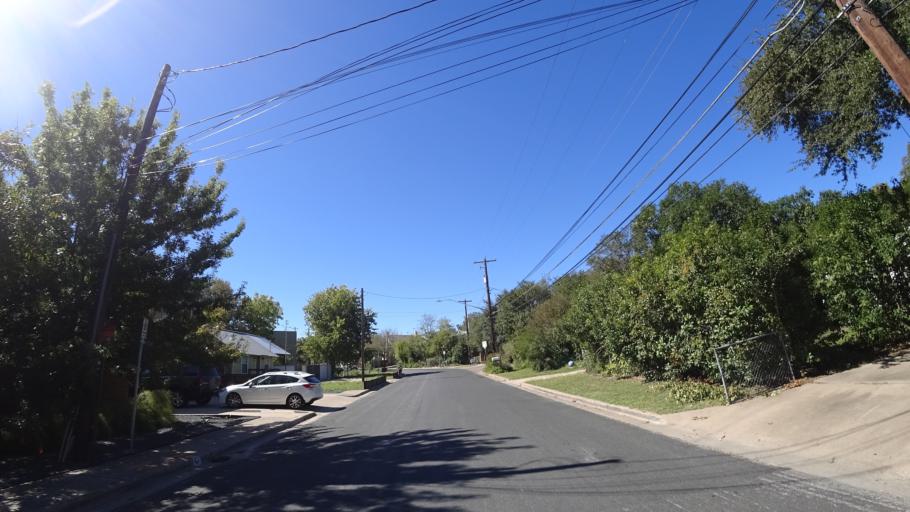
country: US
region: Texas
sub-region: Travis County
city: Austin
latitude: 30.2458
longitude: -97.7711
